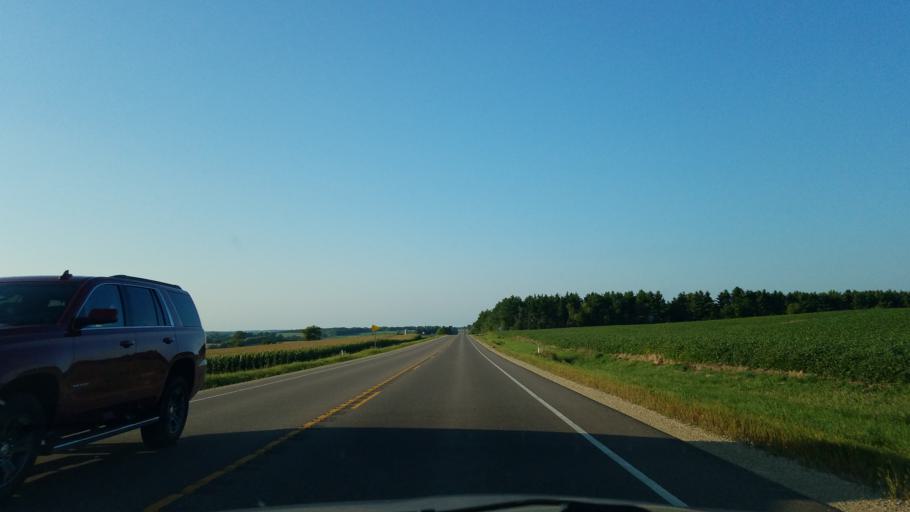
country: US
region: Wisconsin
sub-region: Saint Croix County
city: Baldwin
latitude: 45.0902
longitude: -92.3754
